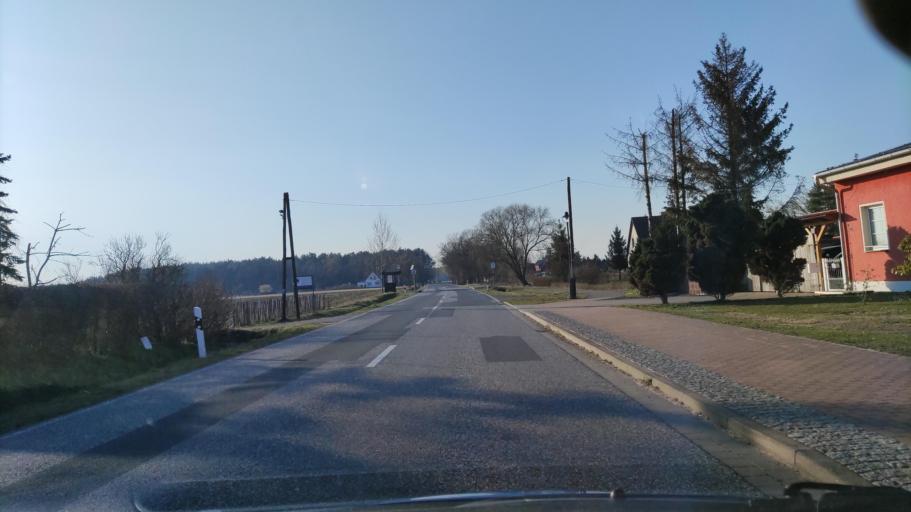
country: DE
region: Saxony-Anhalt
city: Seehausen
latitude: 52.9156
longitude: 11.7159
